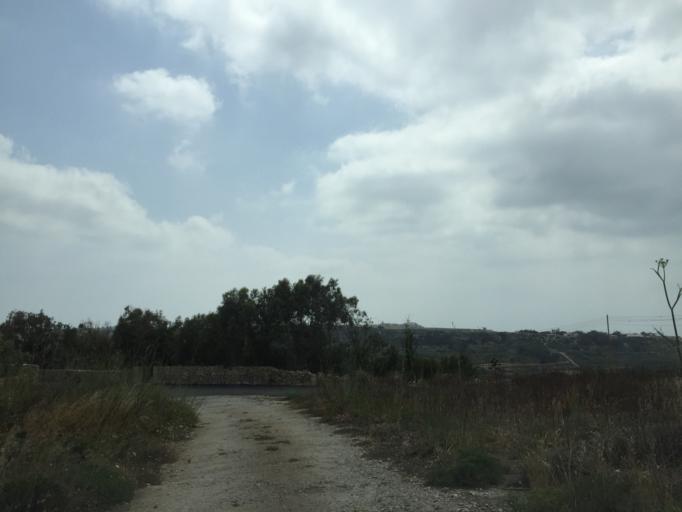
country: MT
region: L-Imgarr
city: Imgarr
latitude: 35.9029
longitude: 14.3626
